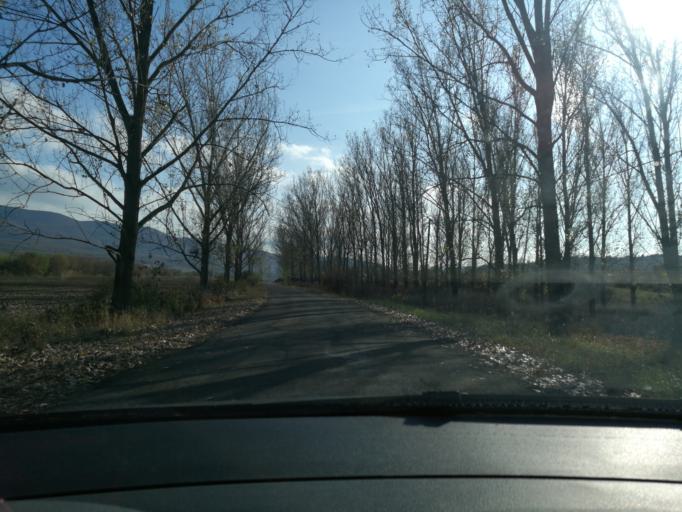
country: HU
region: Nograd
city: Paszto
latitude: 47.9034
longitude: 19.6875
